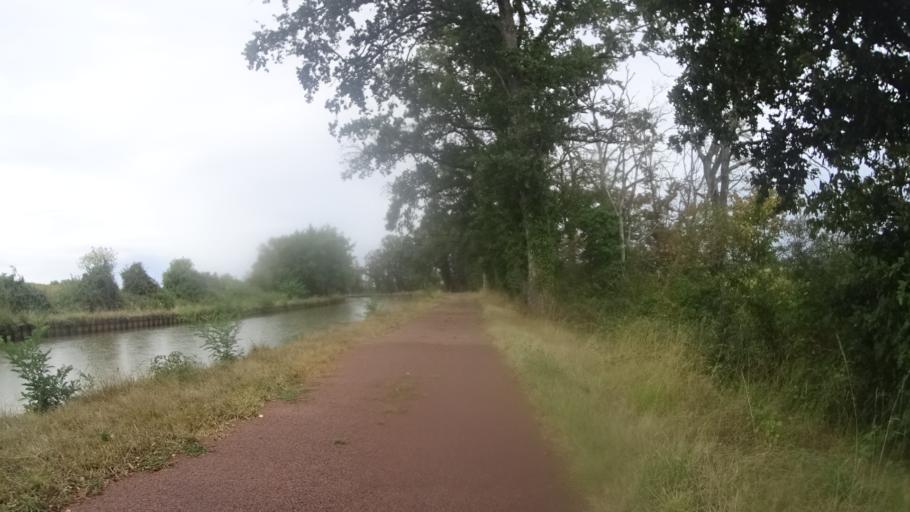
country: FR
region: Bourgogne
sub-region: Departement de la Nievre
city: Imphy
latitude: 46.8639
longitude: 3.2862
